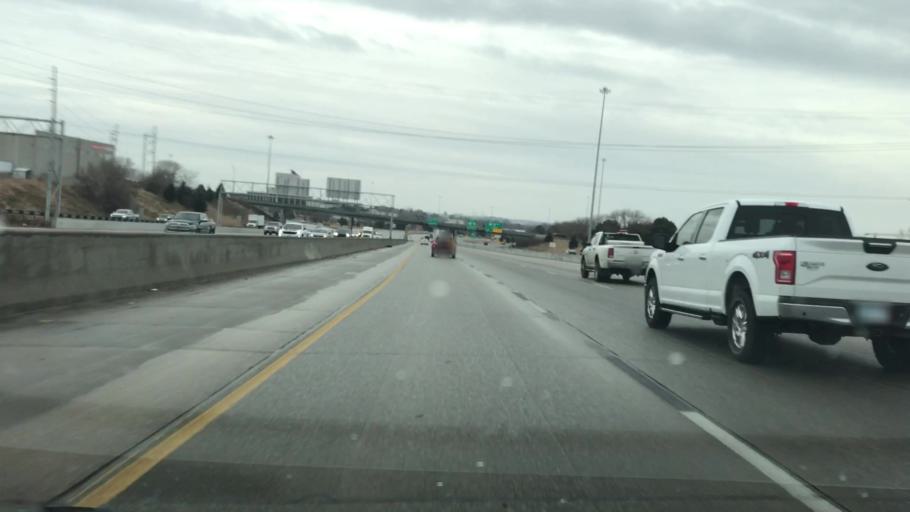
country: US
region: Nebraska
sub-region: Douglas County
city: Ralston
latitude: 41.2191
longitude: -96.0914
